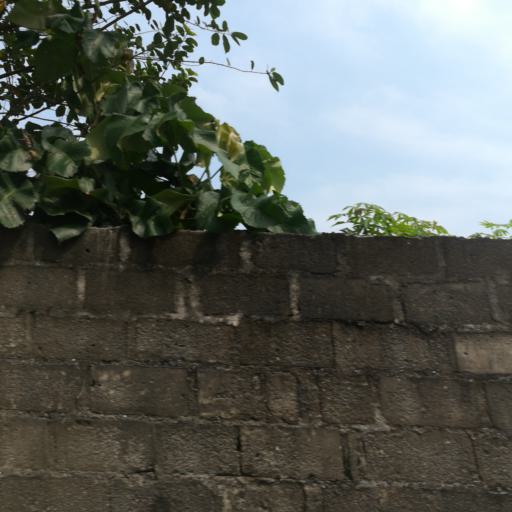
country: NG
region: Rivers
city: Port Harcourt
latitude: 4.8372
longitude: 7.0665
